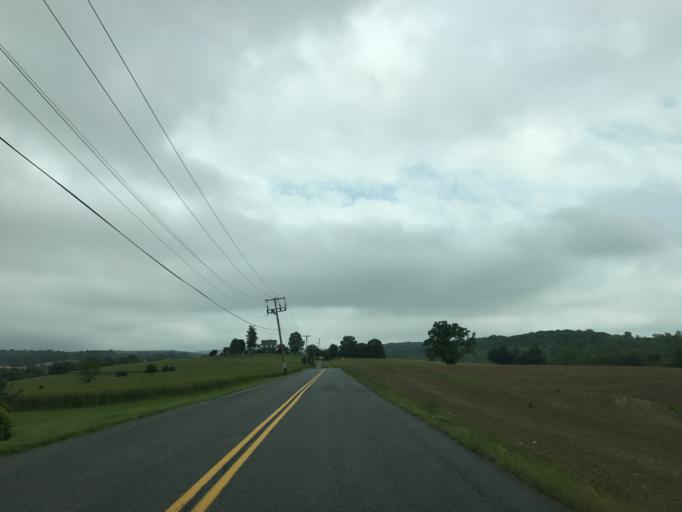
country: US
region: Maryland
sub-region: Harford County
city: Jarrettsville
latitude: 39.6669
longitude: -76.4469
